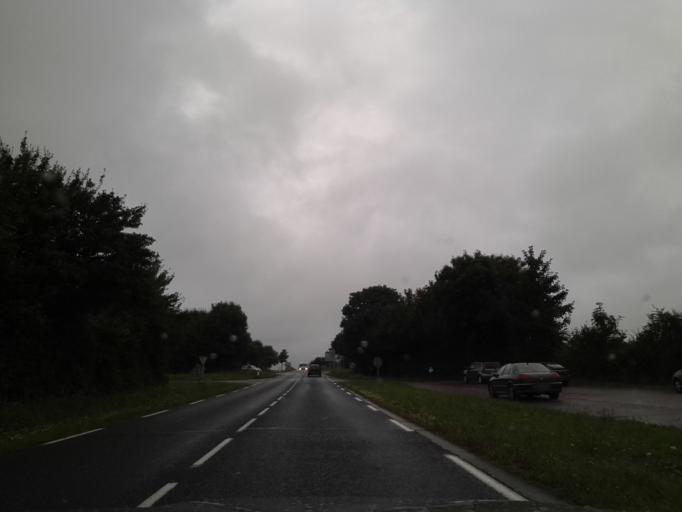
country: FR
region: Lower Normandy
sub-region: Departement de la Manche
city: Carentan
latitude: 49.3334
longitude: -1.2647
